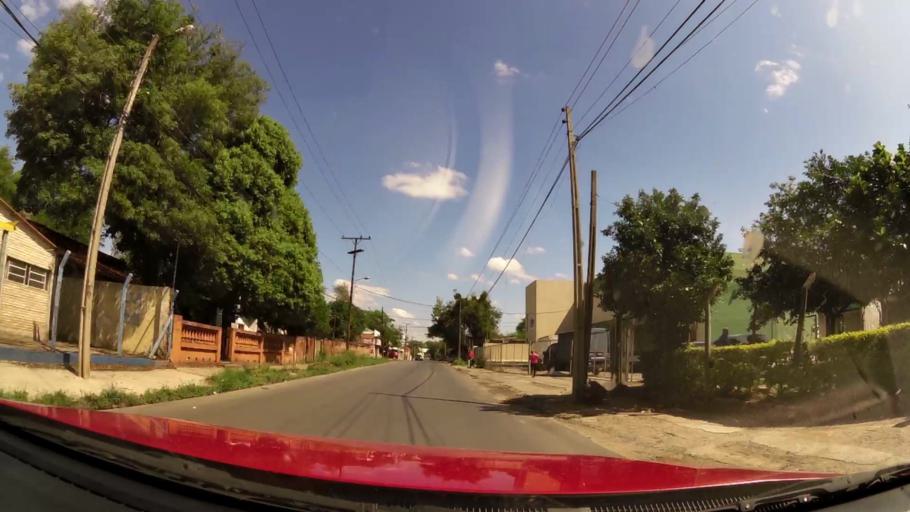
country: PY
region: Central
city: Colonia Mariano Roque Alonso
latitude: -25.2518
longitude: -57.5535
